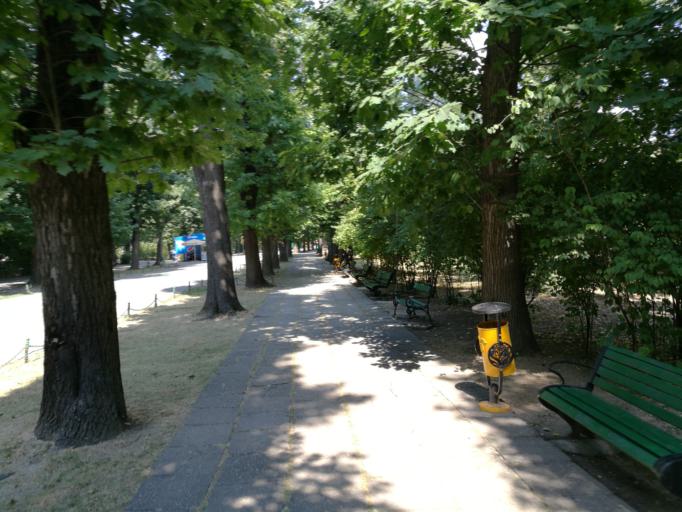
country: RO
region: Bucuresti
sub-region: Municipiul Bucuresti
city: Bucuresti
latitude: 44.4691
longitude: 26.0803
